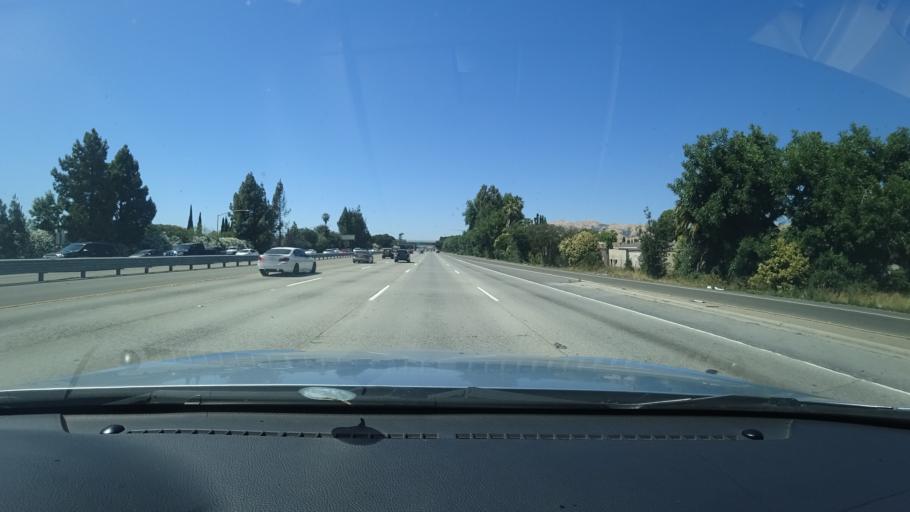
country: US
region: California
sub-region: Santa Clara County
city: Milpitas
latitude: 37.4024
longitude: -121.8765
